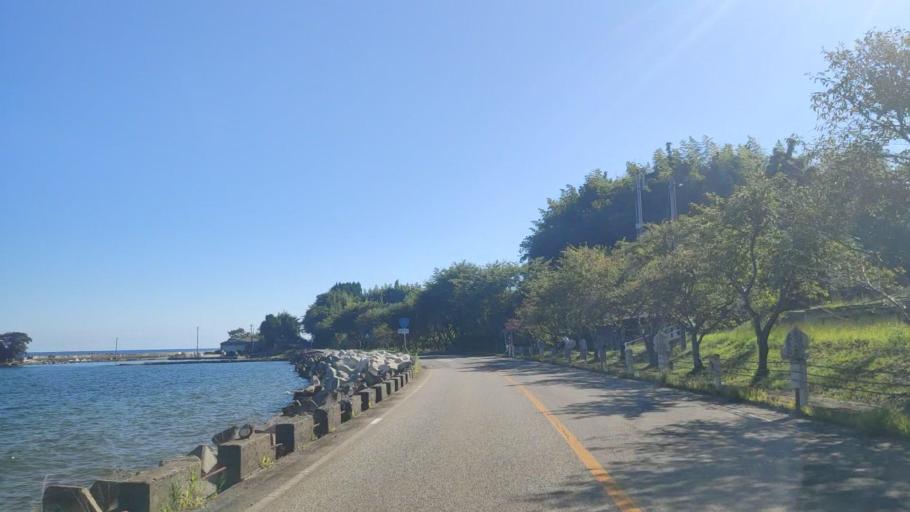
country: JP
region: Ishikawa
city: Nanao
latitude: 37.2764
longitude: 137.0969
